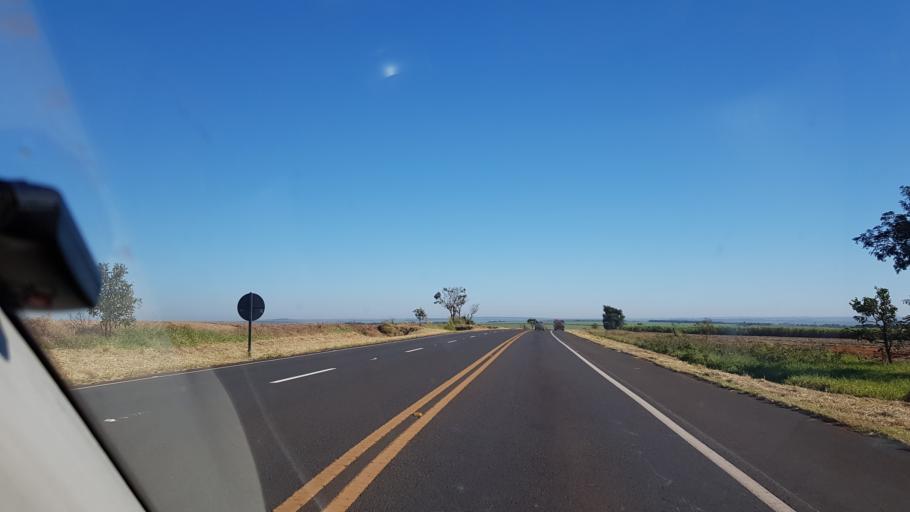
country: BR
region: Sao Paulo
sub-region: Assis
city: Assis
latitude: -22.5722
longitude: -50.5173
